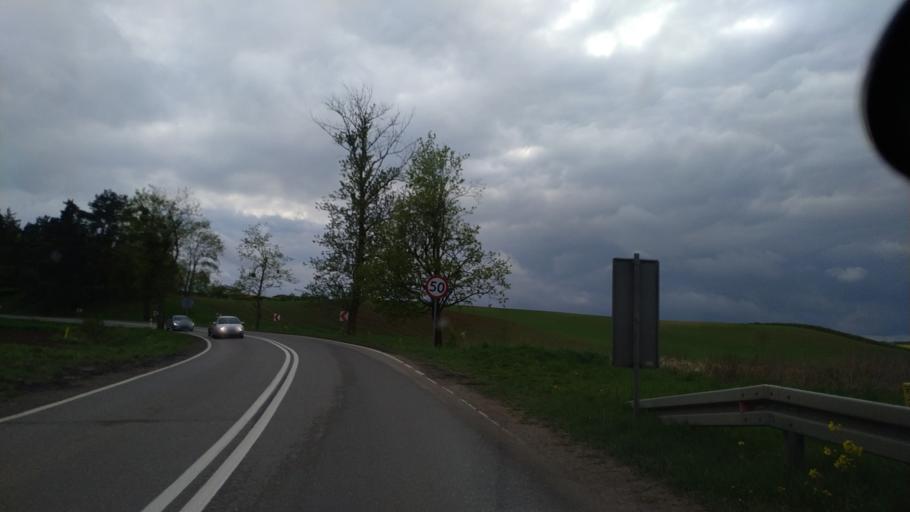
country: PL
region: Pomeranian Voivodeship
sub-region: Powiat kwidzynski
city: Ryjewo
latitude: 53.7978
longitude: 18.9635
